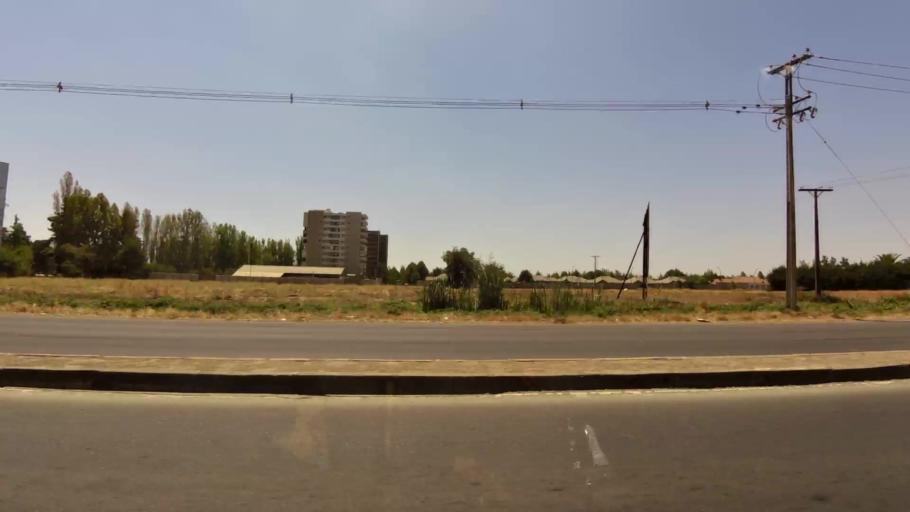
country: CL
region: Maule
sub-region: Provincia de Talca
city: Talca
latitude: -35.4383
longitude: -71.6172
